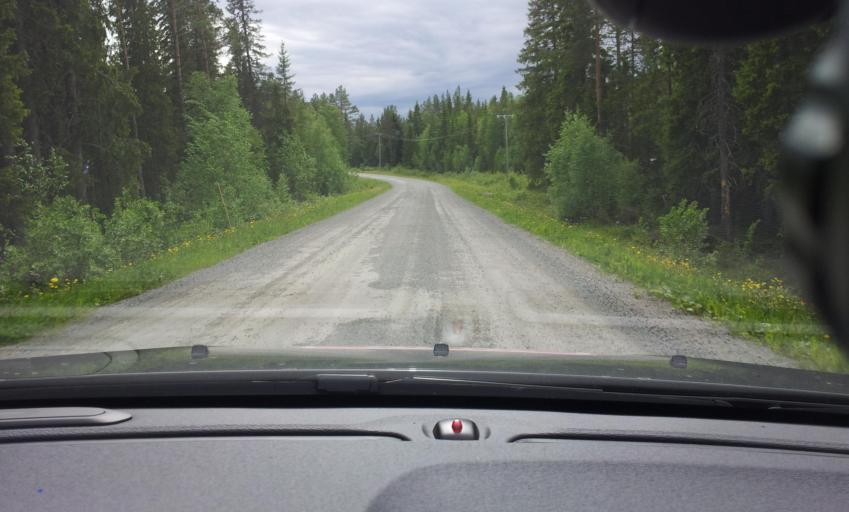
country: SE
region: Jaemtland
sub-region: OEstersunds Kommun
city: Brunflo
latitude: 62.9966
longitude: 14.7368
